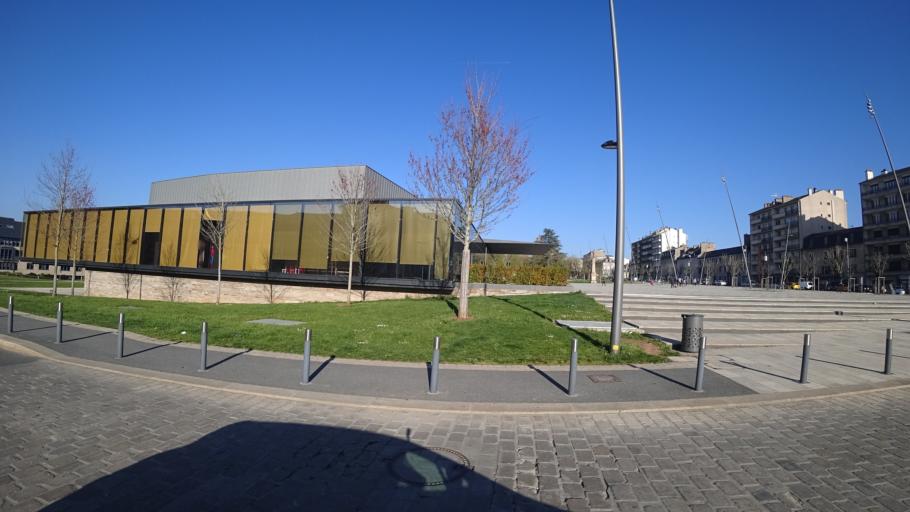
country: FR
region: Midi-Pyrenees
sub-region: Departement de l'Aveyron
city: Rodez
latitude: 44.3520
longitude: 2.5656
